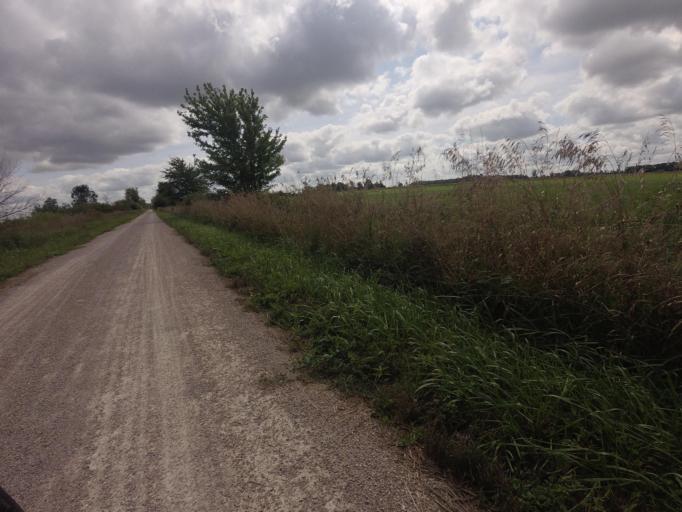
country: CA
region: Ontario
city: North Perth
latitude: 43.5835
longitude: -81.0658
